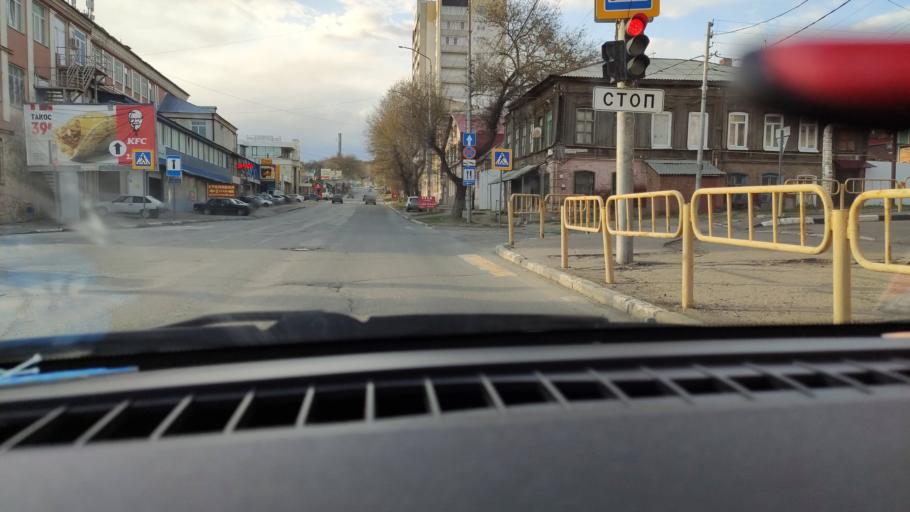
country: RU
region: Saratov
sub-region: Saratovskiy Rayon
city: Saratov
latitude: 51.5375
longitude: 46.0562
